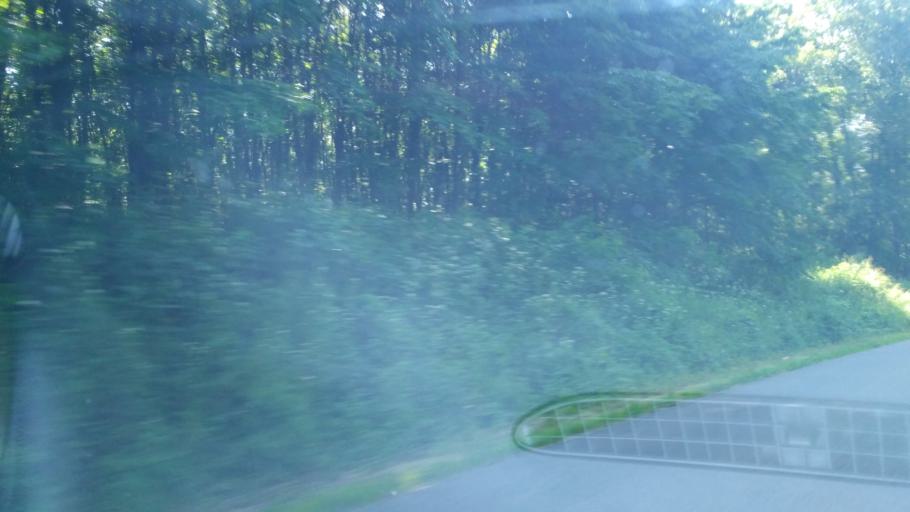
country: PL
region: Subcarpathian Voivodeship
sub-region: Powiat jaroslawski
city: Rokietnica
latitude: 49.9296
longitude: 22.6764
